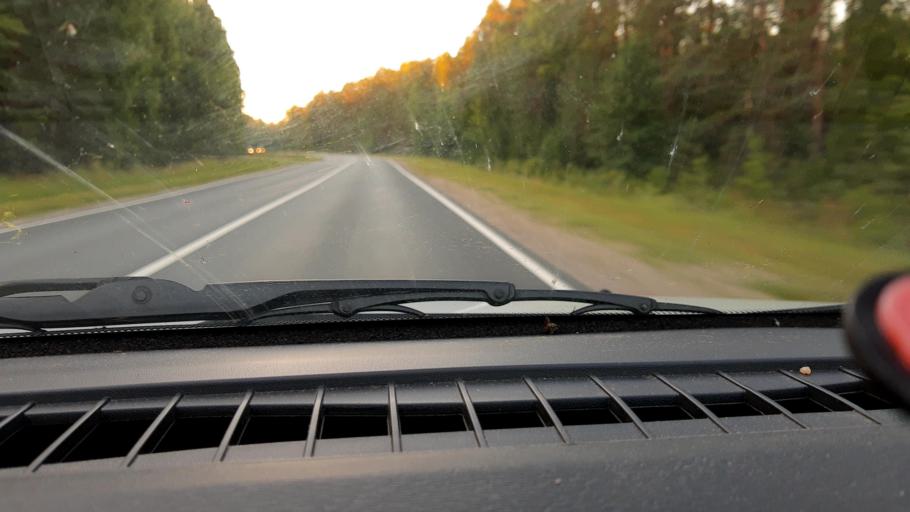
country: RU
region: Nizjnij Novgorod
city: Krasnyye Baki
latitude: 57.2182
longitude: 45.4838
